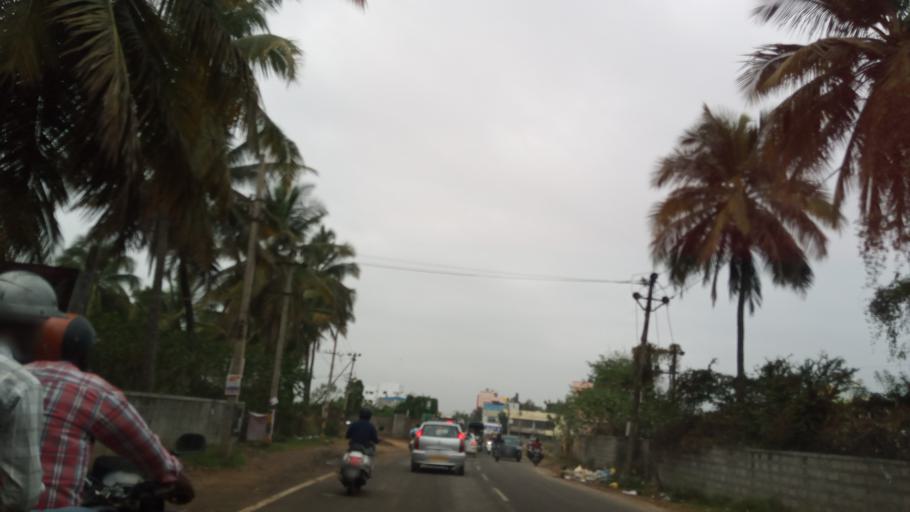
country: IN
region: Karnataka
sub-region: Bangalore Urban
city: Bangalore
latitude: 12.9043
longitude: 77.5265
